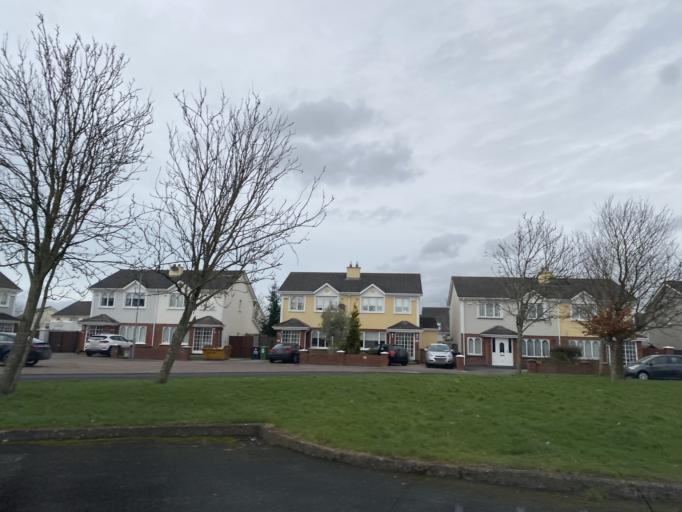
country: IE
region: Leinster
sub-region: Kildare
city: Celbridge
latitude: 53.3498
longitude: -6.5552
